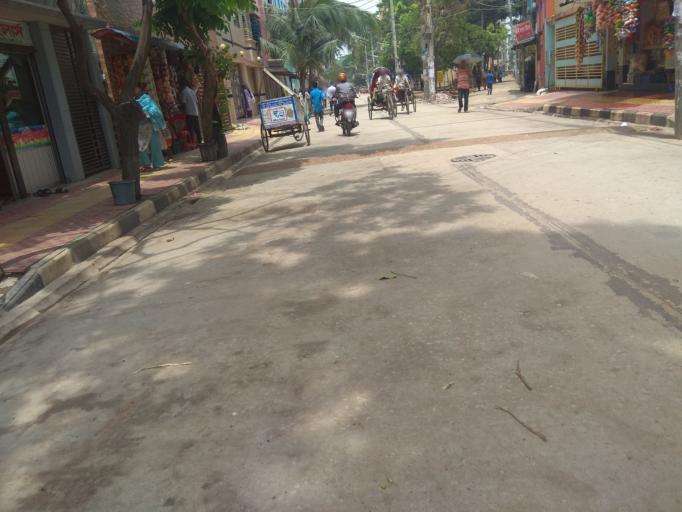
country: BD
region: Dhaka
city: Tungi
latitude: 23.8172
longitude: 90.3551
